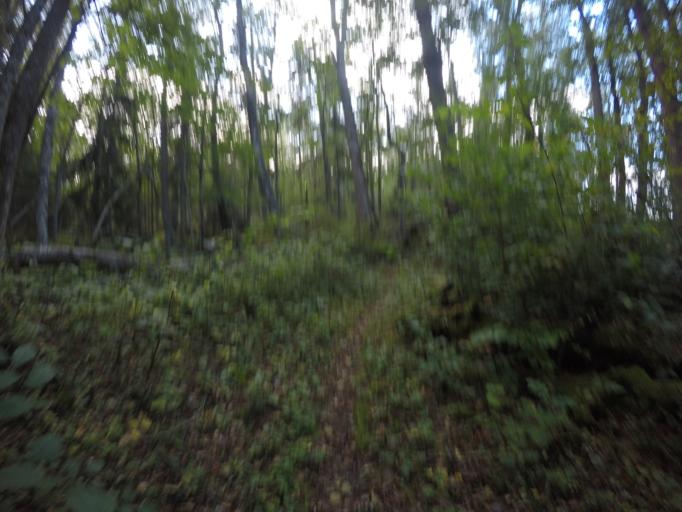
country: SE
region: Vaestmanland
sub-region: Hallstahammars Kommun
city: Kolback
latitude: 59.4816
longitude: 16.2337
